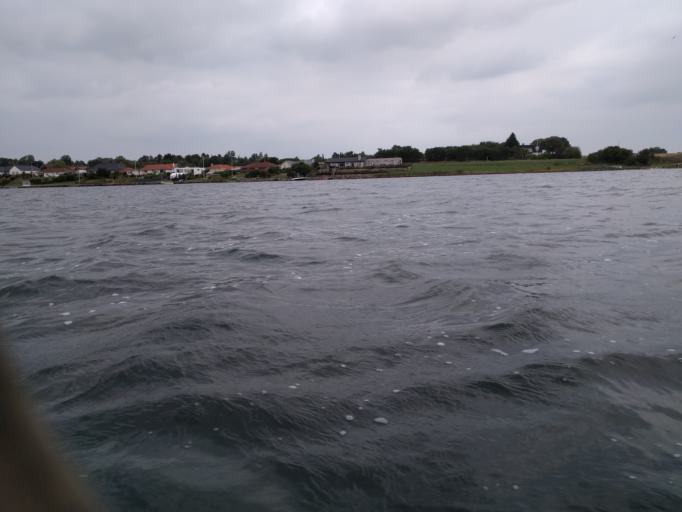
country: DK
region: South Denmark
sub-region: Kerteminde Kommune
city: Munkebo
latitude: 55.4596
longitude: 10.5903
